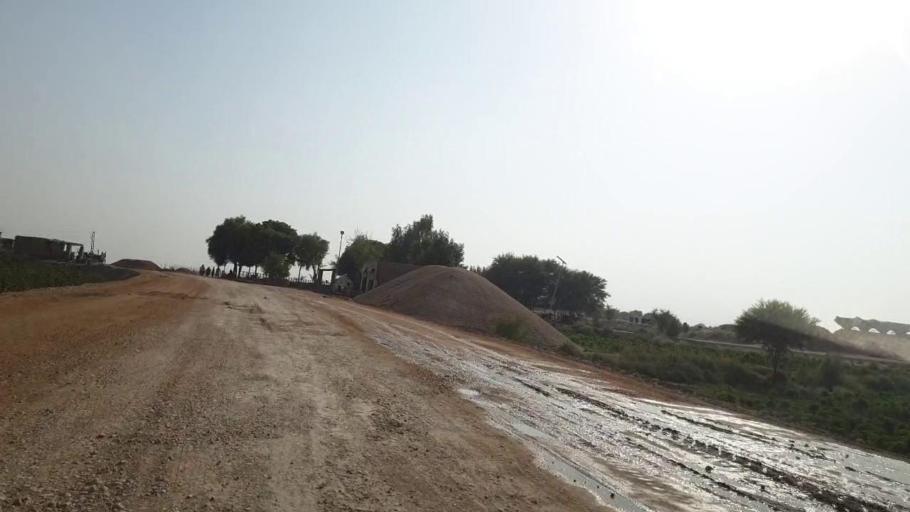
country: PK
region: Sindh
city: Bhan
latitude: 26.5024
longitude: 67.7823
